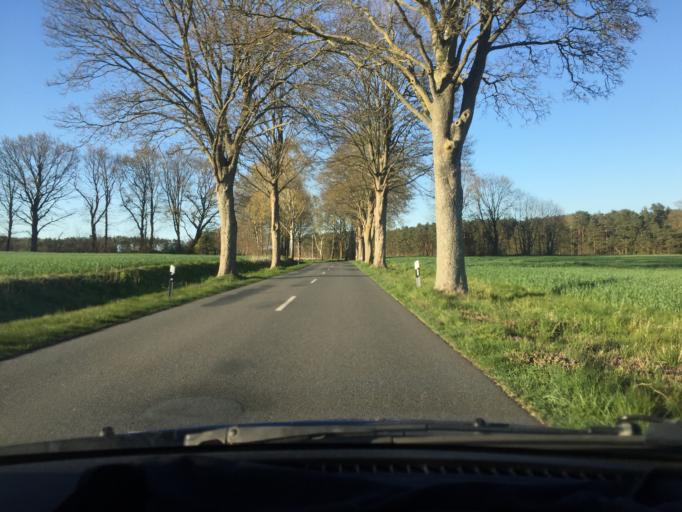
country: DE
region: Lower Saxony
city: Himbergen
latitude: 53.0682
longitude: 10.7274
